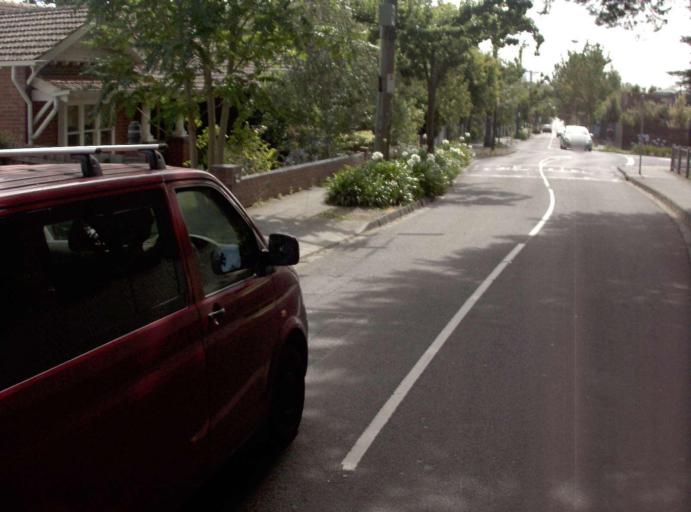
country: AU
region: Victoria
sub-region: Boroondara
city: Hawthorn East
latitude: -37.8196
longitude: 145.0424
